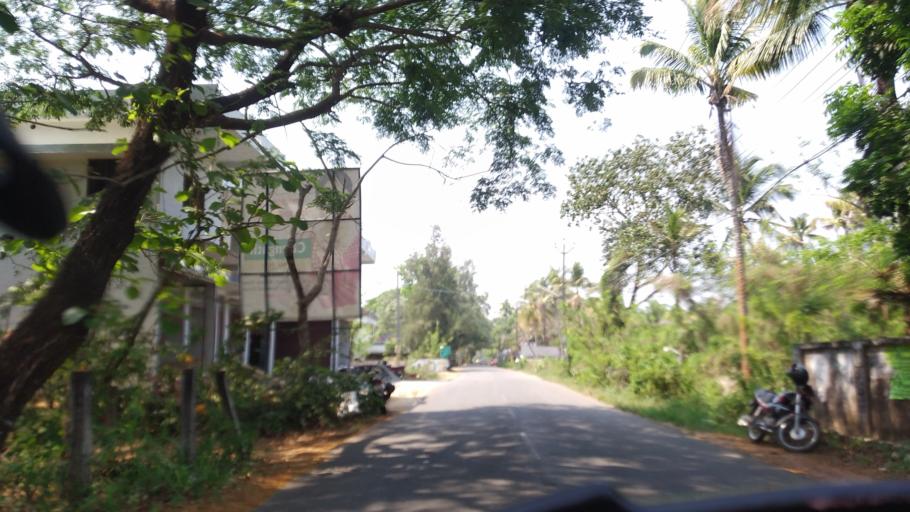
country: IN
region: Kerala
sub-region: Thrissur District
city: Kodungallur
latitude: 10.2541
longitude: 76.1470
